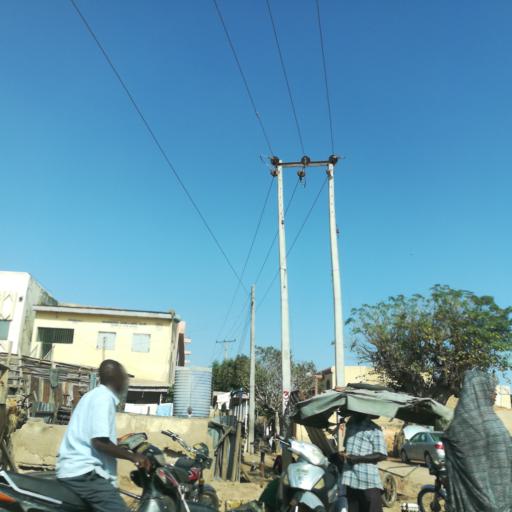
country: NG
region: Kano
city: Kano
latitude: 12.0172
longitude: 8.5046
